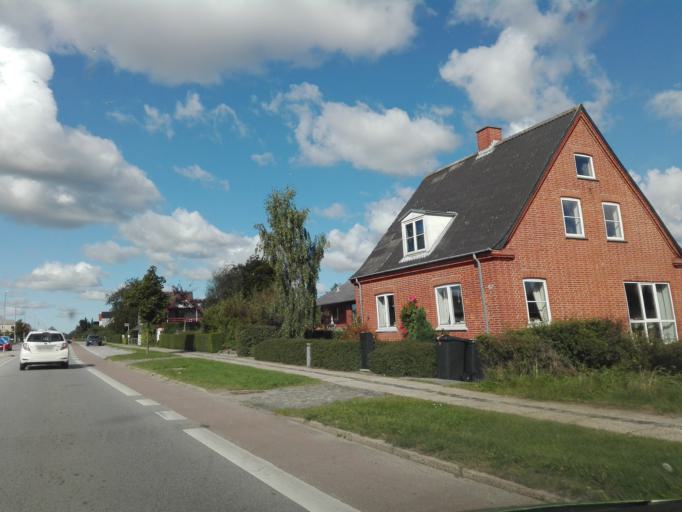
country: DK
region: North Denmark
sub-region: Mariagerfjord Kommune
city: Hobro
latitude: 56.6282
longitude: 9.8029
